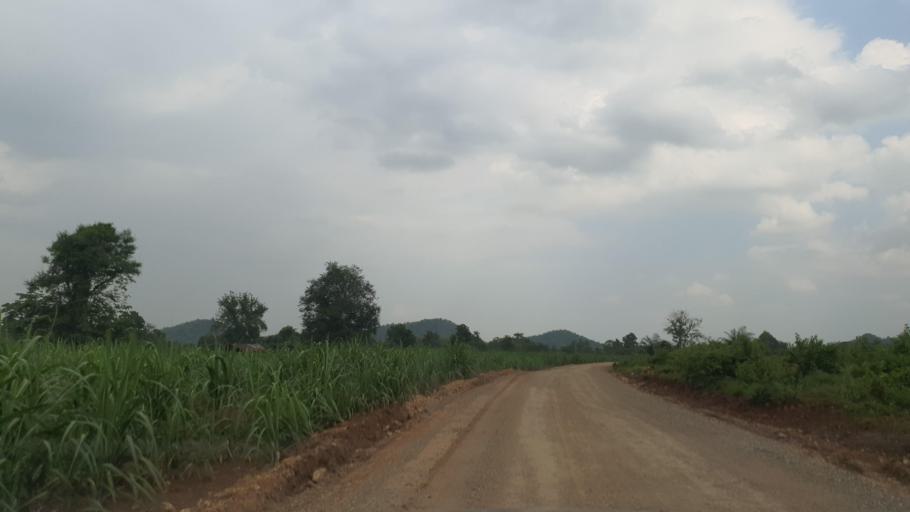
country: TH
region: Sukhothai
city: Thung Saliam
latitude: 17.2548
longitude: 99.5421
